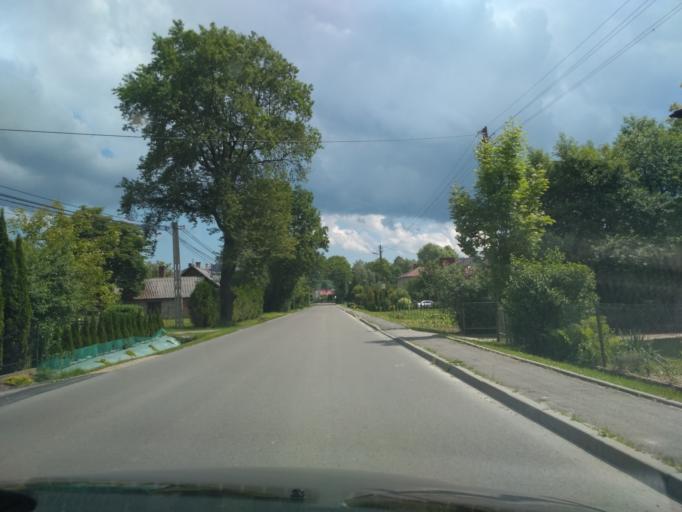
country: PL
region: Subcarpathian Voivodeship
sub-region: Powiat rzeszowski
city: Blazowa
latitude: 49.8779
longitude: 22.0828
